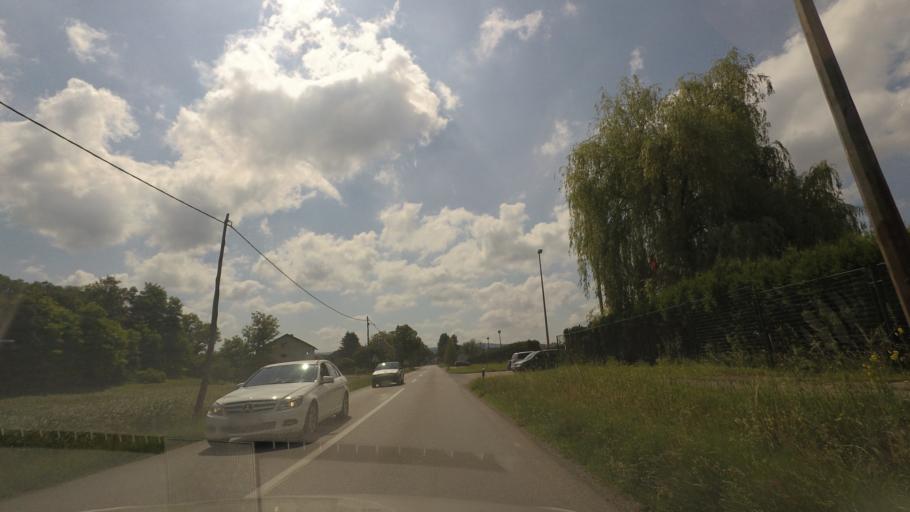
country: HR
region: Karlovacka
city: Vojnic
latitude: 45.3294
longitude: 15.6912
